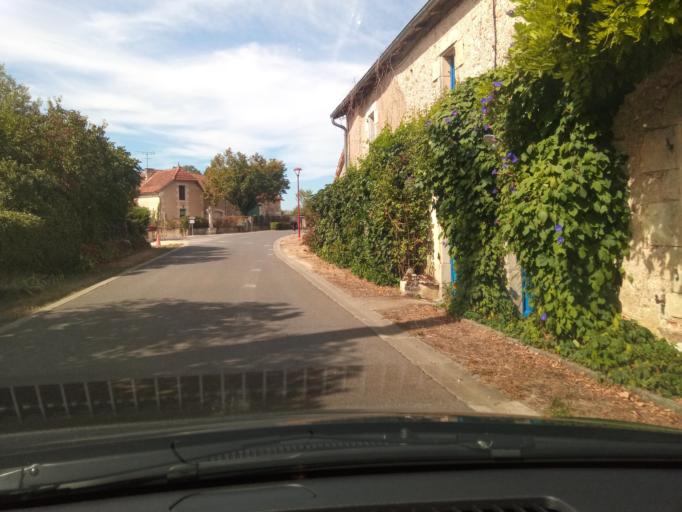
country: FR
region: Poitou-Charentes
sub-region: Departement de la Vienne
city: Chauvigny
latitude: 46.5555
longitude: 0.7449
